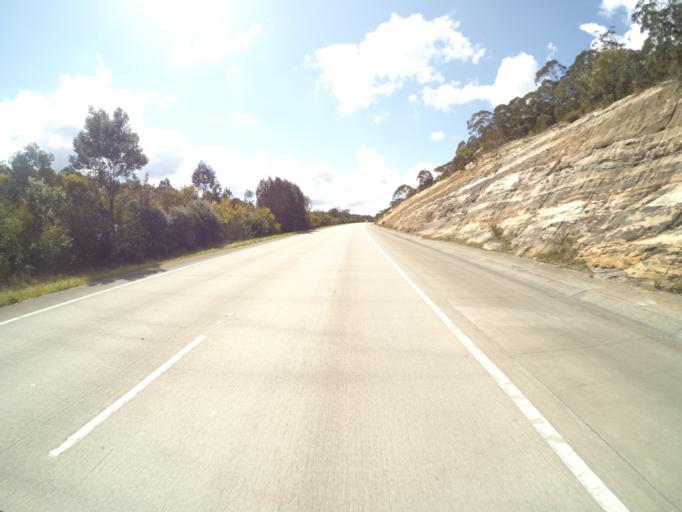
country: AU
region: New South Wales
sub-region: Wingecarribee
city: Colo Vale
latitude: -34.4259
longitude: 150.4696
